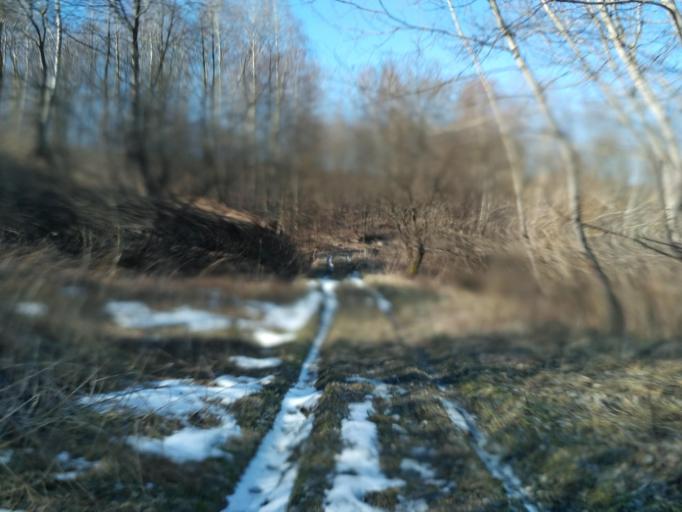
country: PL
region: Subcarpathian Voivodeship
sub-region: Powiat brzozowski
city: Golcowa
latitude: 49.7601
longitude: 22.0318
